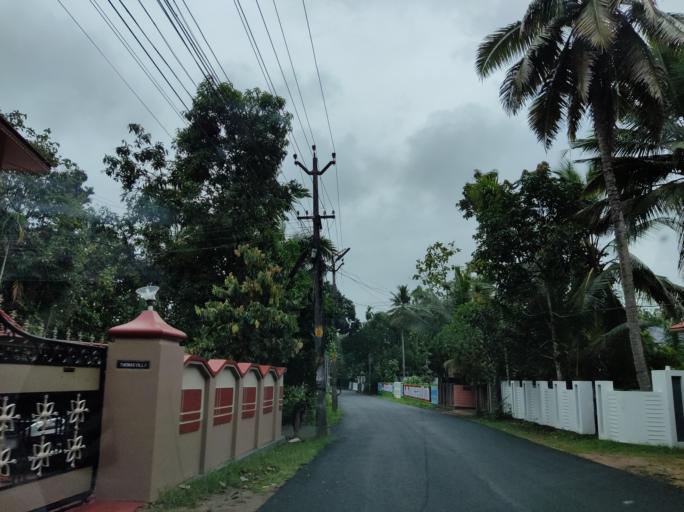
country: IN
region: Kerala
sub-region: Alappuzha
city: Mavelikara
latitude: 9.2460
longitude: 76.5283
